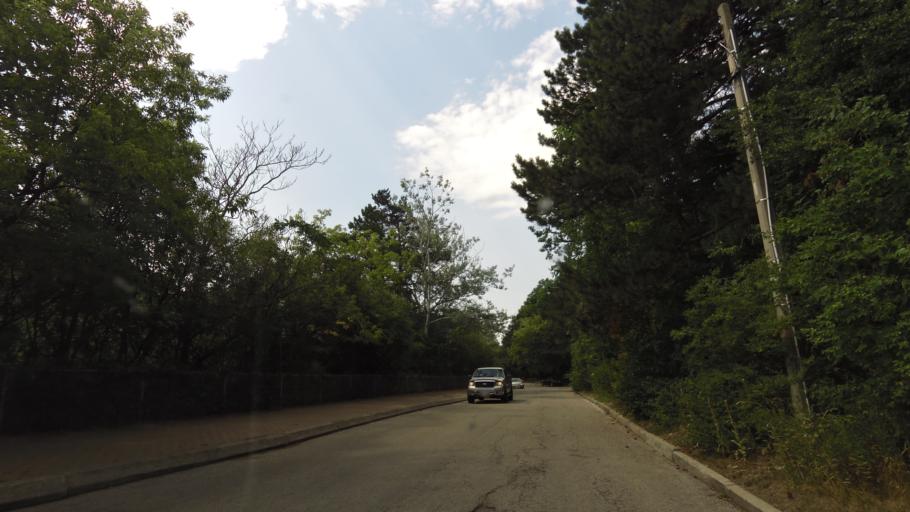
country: CA
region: Ontario
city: Toronto
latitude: 43.6403
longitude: -79.4551
